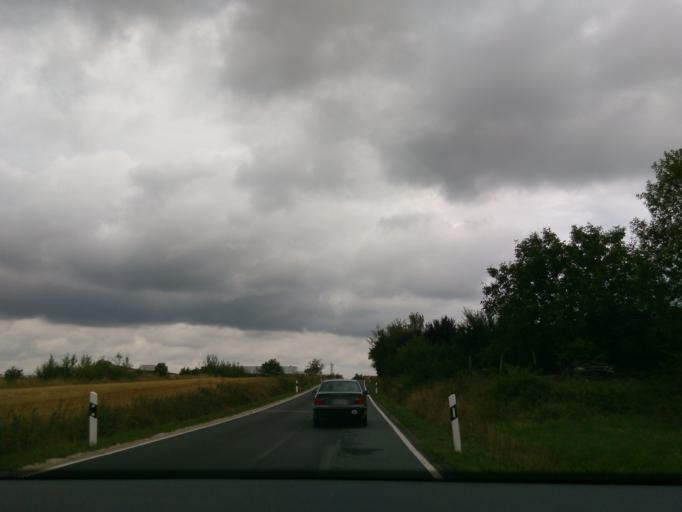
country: DE
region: Bavaria
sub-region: Regierungsbezirk Mittelfranken
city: Hochstadt an der Aisch
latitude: 49.6903
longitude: 10.8037
